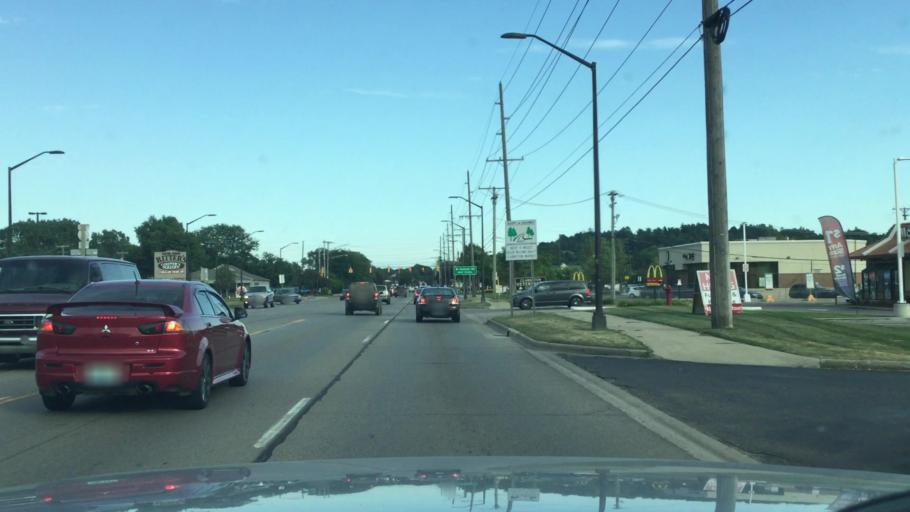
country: US
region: Michigan
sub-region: Oakland County
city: Clarkston
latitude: 42.7194
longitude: -83.4174
